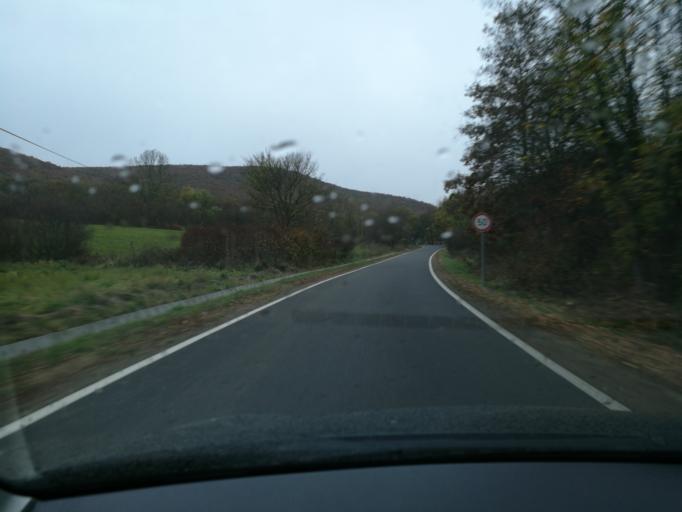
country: HU
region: Nograd
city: Paszto
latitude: 47.9749
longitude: 19.6262
